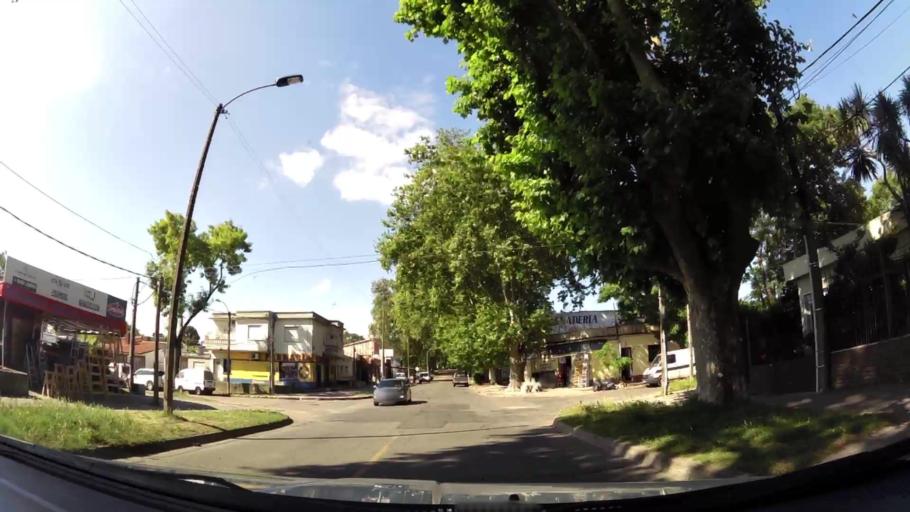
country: UY
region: Montevideo
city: Montevideo
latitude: -34.8456
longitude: -56.2118
